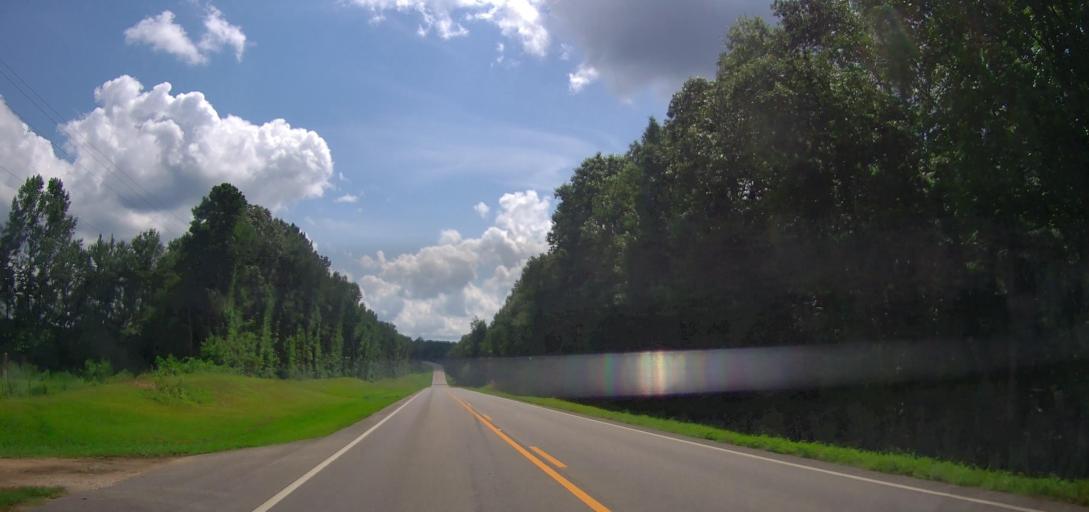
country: US
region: Alabama
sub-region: Cleburne County
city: Heflin
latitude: 33.6059
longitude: -85.4783
